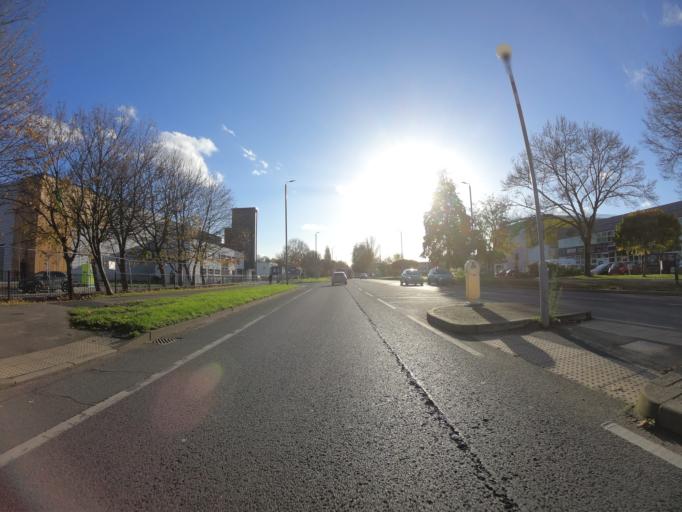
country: GB
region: England
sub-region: Greater London
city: Orpington
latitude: 51.3903
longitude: 0.1104
